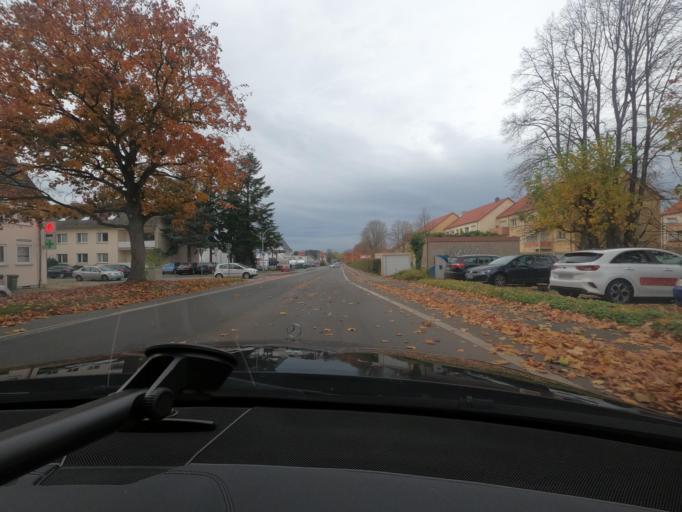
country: DE
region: North Rhine-Westphalia
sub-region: Regierungsbezirk Arnsberg
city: Soest
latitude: 51.5590
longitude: 8.1268
